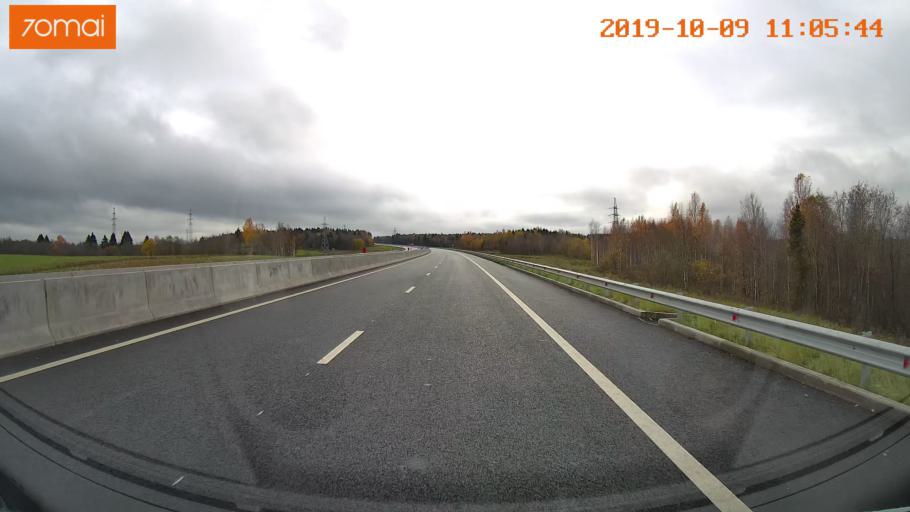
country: RU
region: Vologda
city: Molochnoye
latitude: 59.1958
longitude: 39.7580
